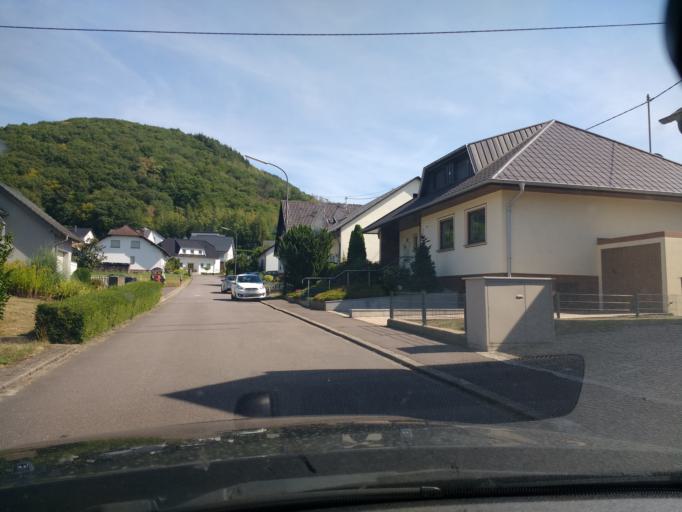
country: DE
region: Rheinland-Pfalz
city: Irsch
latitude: 49.6067
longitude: 6.5990
